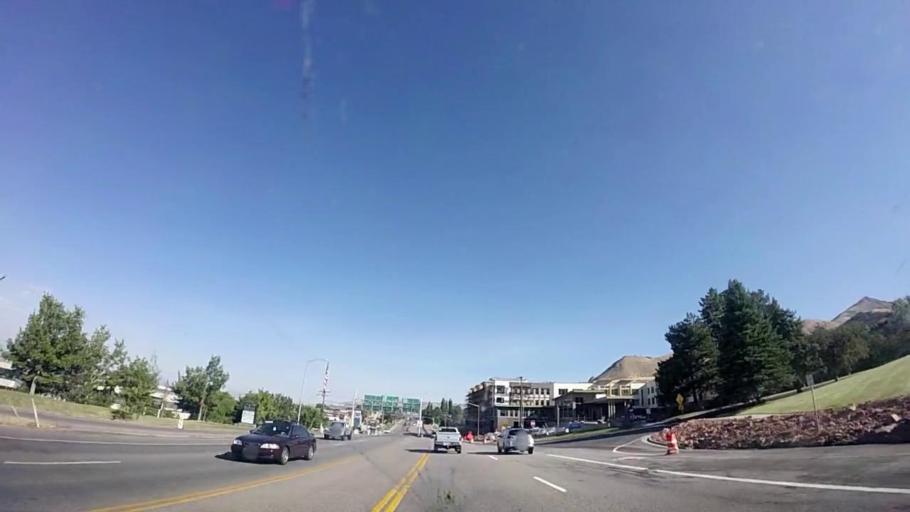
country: US
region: Utah
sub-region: Salt Lake County
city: Canyon Rim
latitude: 40.7188
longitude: -111.8100
